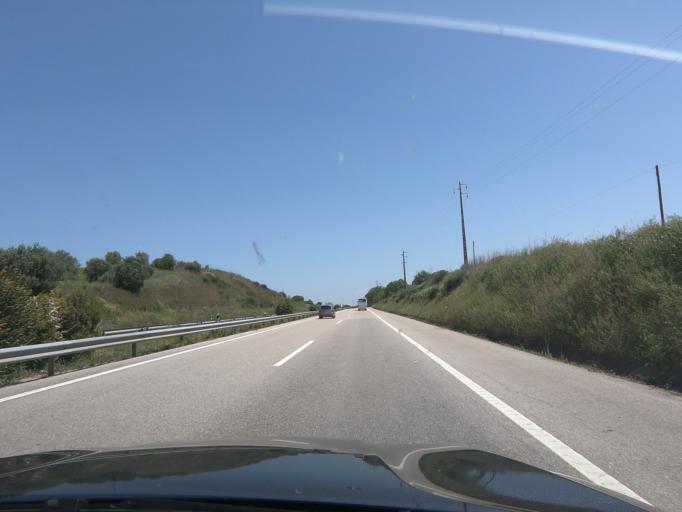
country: PT
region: Santarem
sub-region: Torres Novas
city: Torres Novas
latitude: 39.4659
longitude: -8.5579
